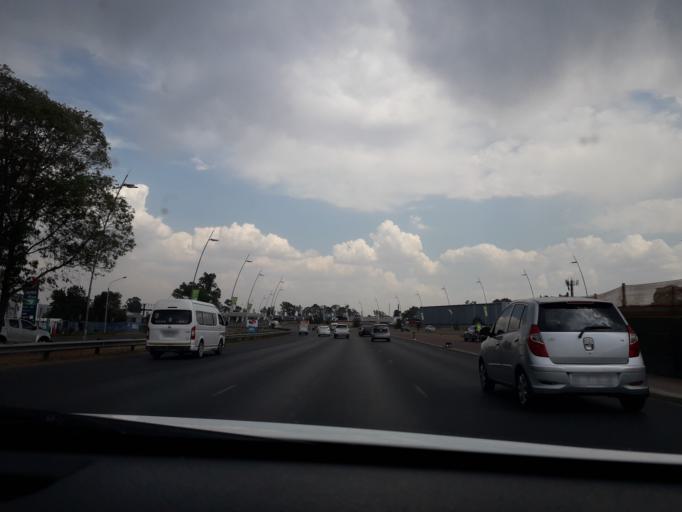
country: ZA
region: Gauteng
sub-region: City of Johannesburg Metropolitan Municipality
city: Modderfontein
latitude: -26.0704
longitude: 28.1860
